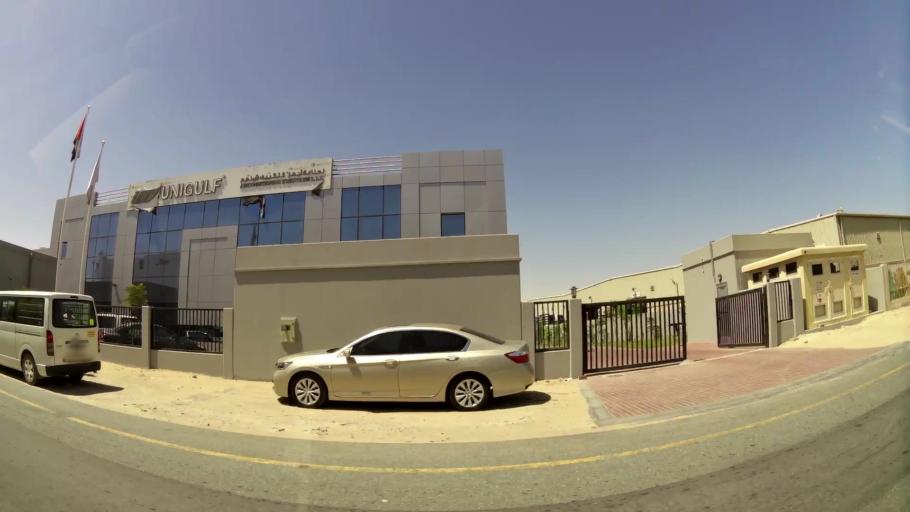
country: AE
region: Dubai
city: Dubai
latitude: 24.9879
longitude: 55.2083
